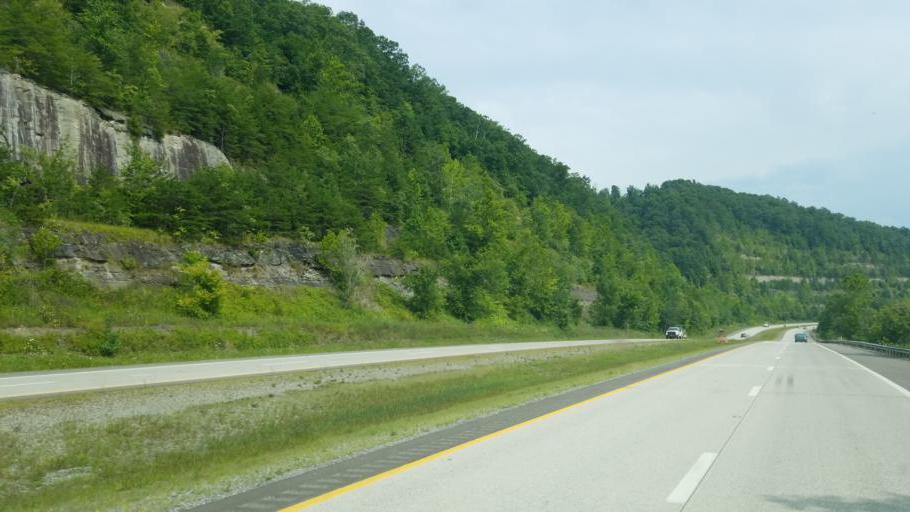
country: US
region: West Virginia
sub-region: Kanawha County
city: Alum Creek
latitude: 38.2174
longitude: -81.8336
